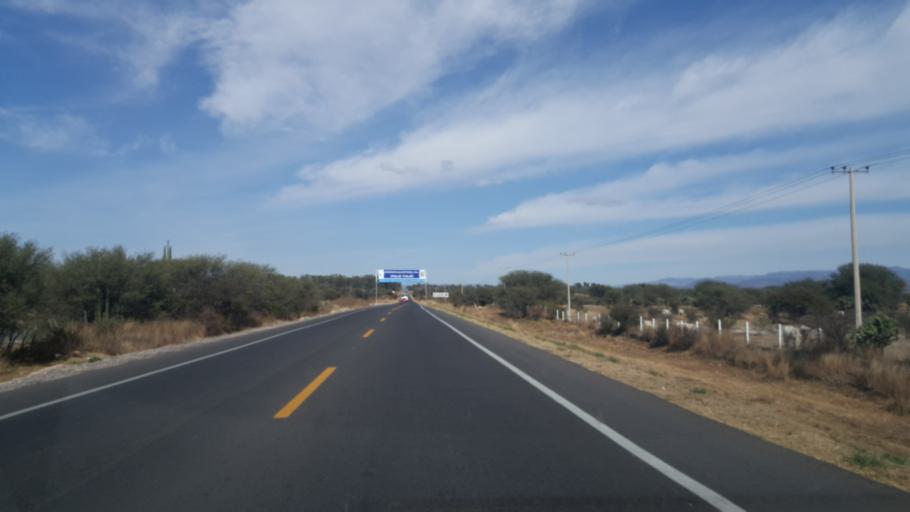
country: MX
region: Jalisco
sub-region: Lagos de Moreno
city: Cristeros [Fraccionamiento]
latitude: 21.2692
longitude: -101.9427
